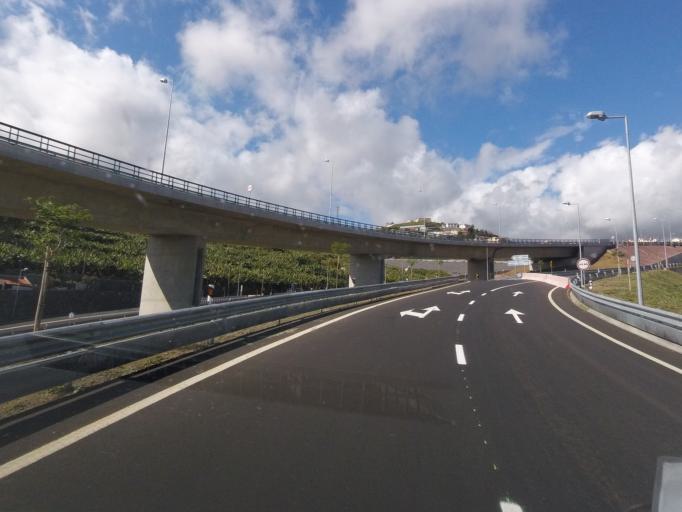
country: PT
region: Madeira
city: Camara de Lobos
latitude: 32.6593
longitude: -16.9693
